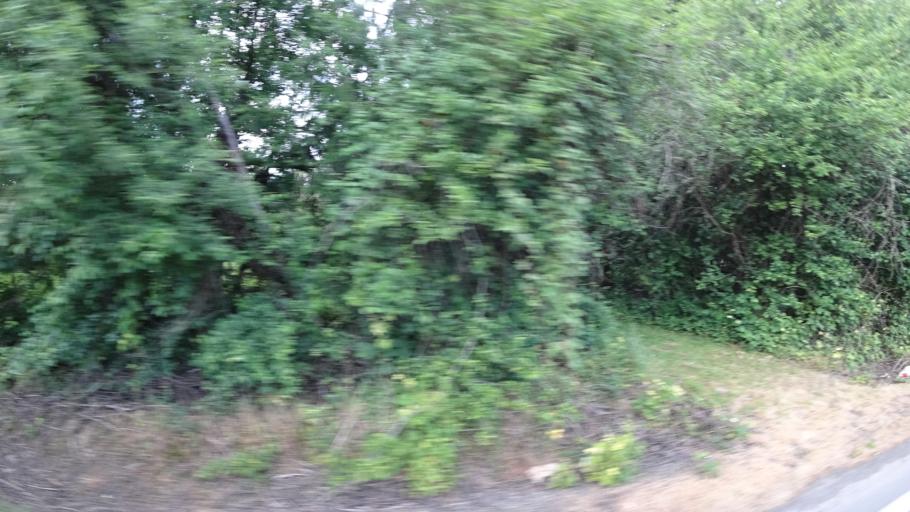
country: US
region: Oregon
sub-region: Clackamas County
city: Damascus
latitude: 45.4653
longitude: -122.4780
